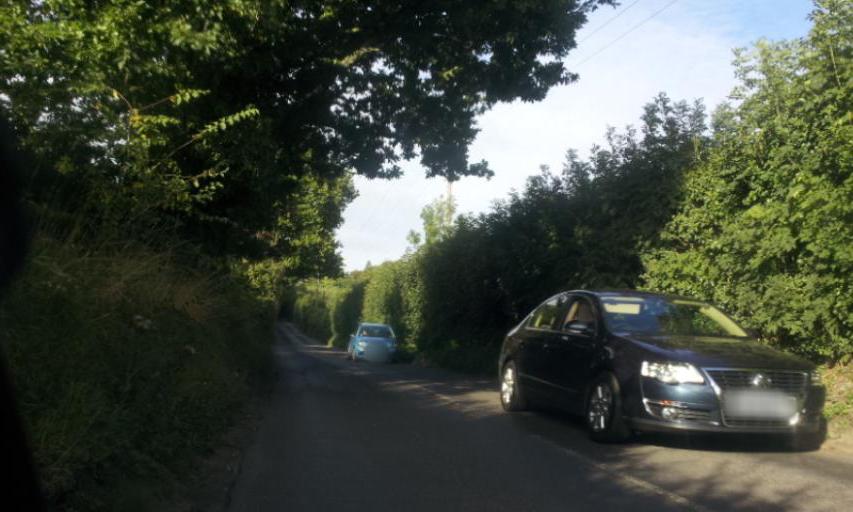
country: GB
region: England
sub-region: Kent
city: Yalding
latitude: 51.2274
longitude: 0.4740
